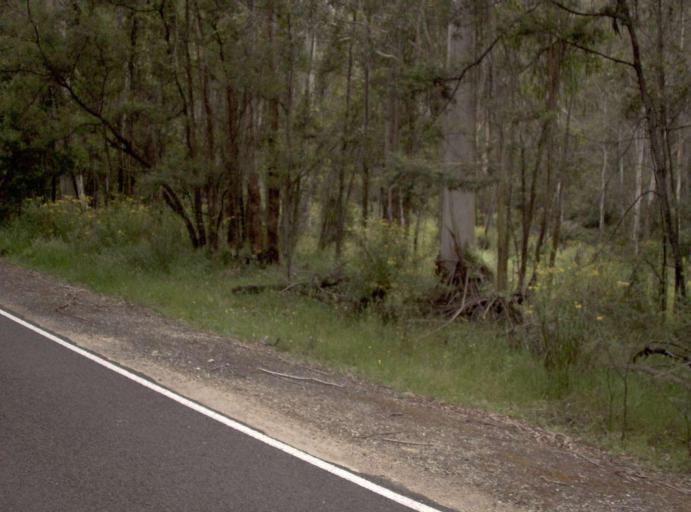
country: AU
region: New South Wales
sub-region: Bombala
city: Bombala
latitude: -37.4239
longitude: 149.2006
